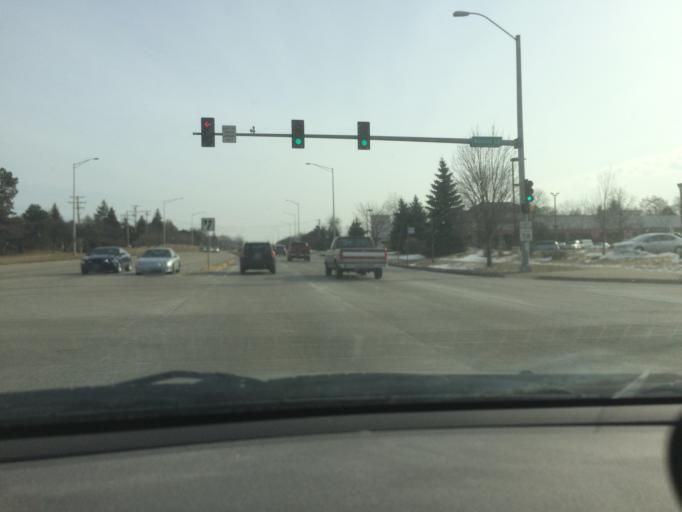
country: US
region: Illinois
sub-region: Cook County
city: South Barrington
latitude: 42.0473
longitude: -88.1265
